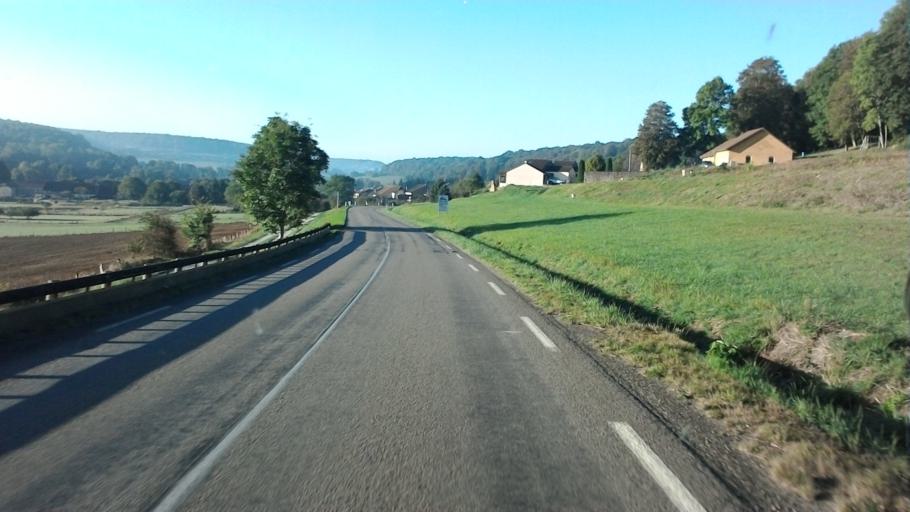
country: FR
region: Lorraine
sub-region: Departement des Vosges
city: Liffol-le-Grand
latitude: 48.2426
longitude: 5.6113
